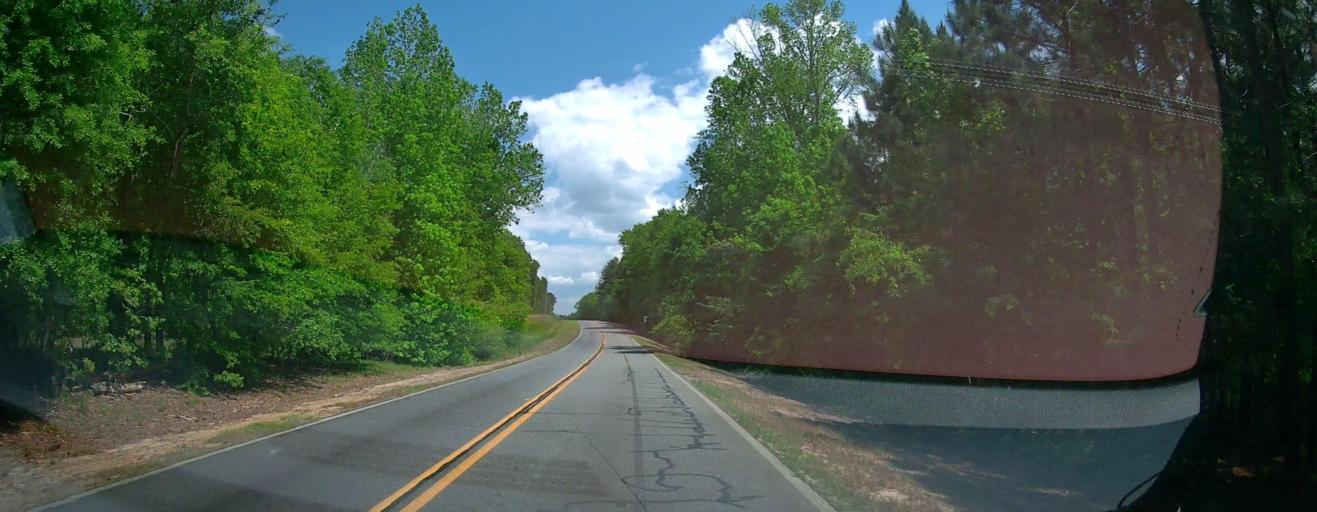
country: US
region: Georgia
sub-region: Treutlen County
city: Soperton
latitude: 32.5095
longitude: -82.6408
